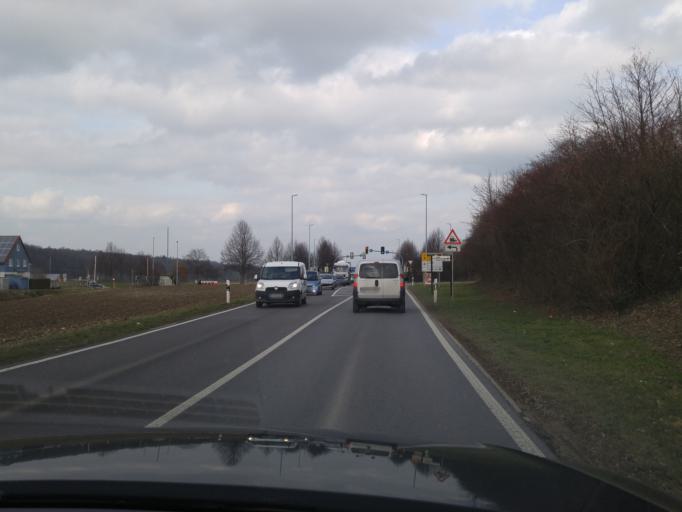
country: DE
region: Baden-Wuerttemberg
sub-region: Regierungsbezirk Stuttgart
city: Owen
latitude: 48.5919
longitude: 9.4489
